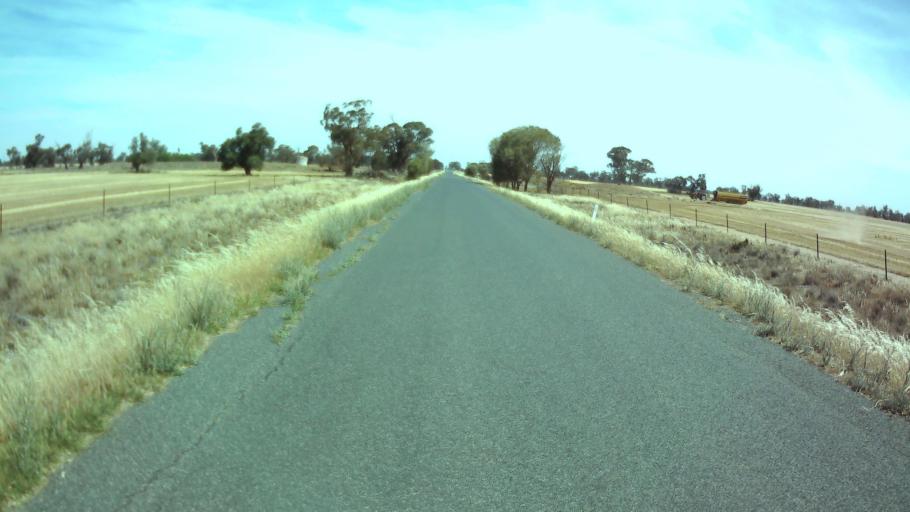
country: AU
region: New South Wales
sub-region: Weddin
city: Grenfell
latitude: -33.9922
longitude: 147.7758
